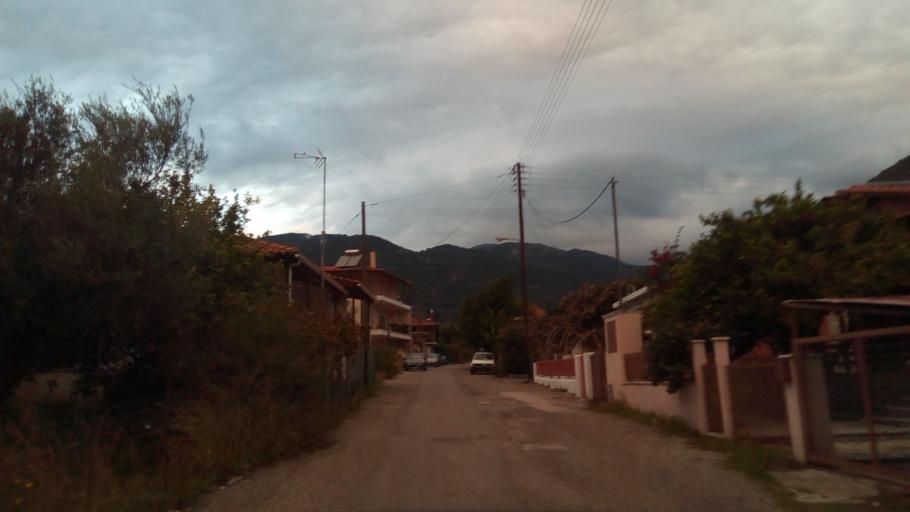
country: GR
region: West Greece
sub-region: Nomos Aitolias kai Akarnanias
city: Nafpaktos
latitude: 38.4099
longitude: 21.8493
